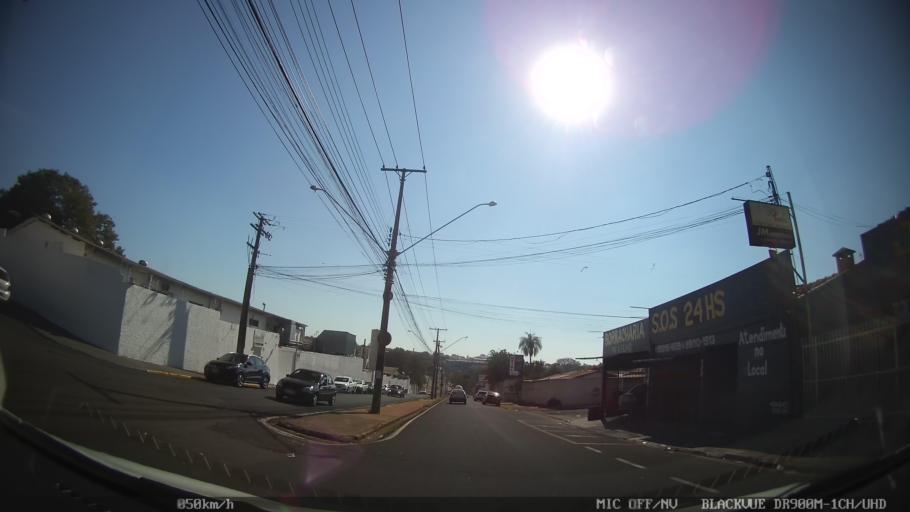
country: BR
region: Sao Paulo
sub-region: Sao Jose Do Rio Preto
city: Sao Jose do Rio Preto
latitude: -20.7800
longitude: -49.3863
